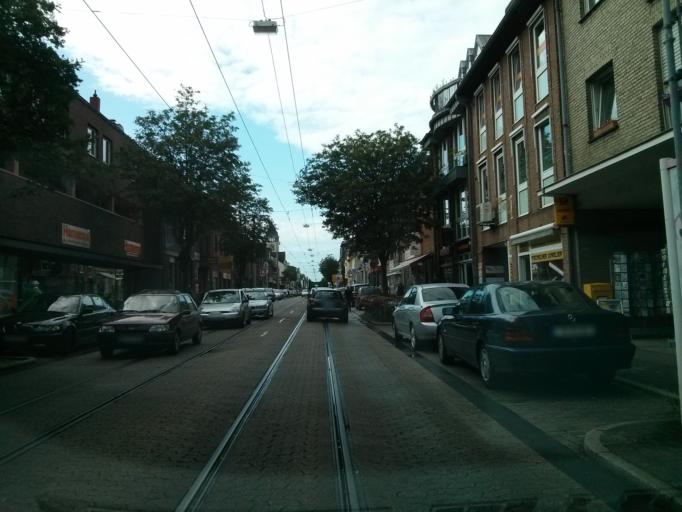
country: DE
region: North Rhine-Westphalia
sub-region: Regierungsbezirk Dusseldorf
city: Krefeld
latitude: 51.3040
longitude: 6.5887
